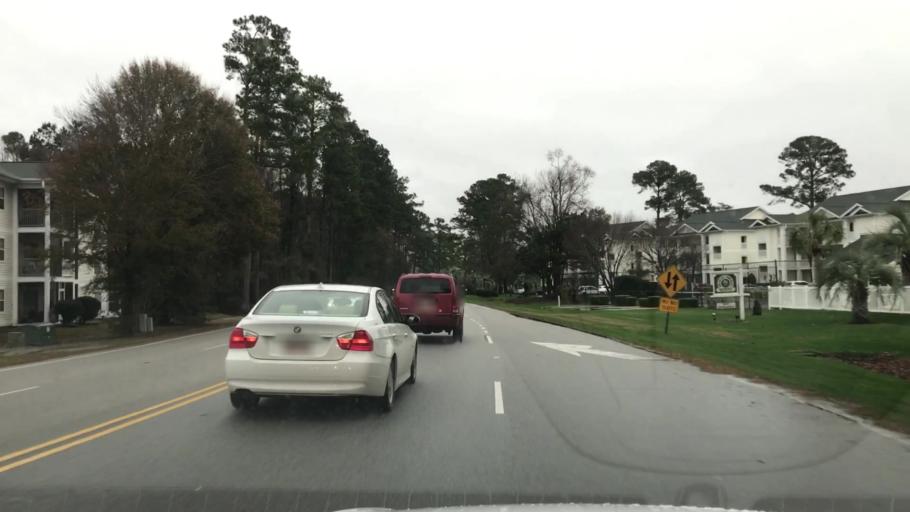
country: US
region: South Carolina
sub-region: Horry County
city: Forestbrook
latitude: 33.7234
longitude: -78.9199
